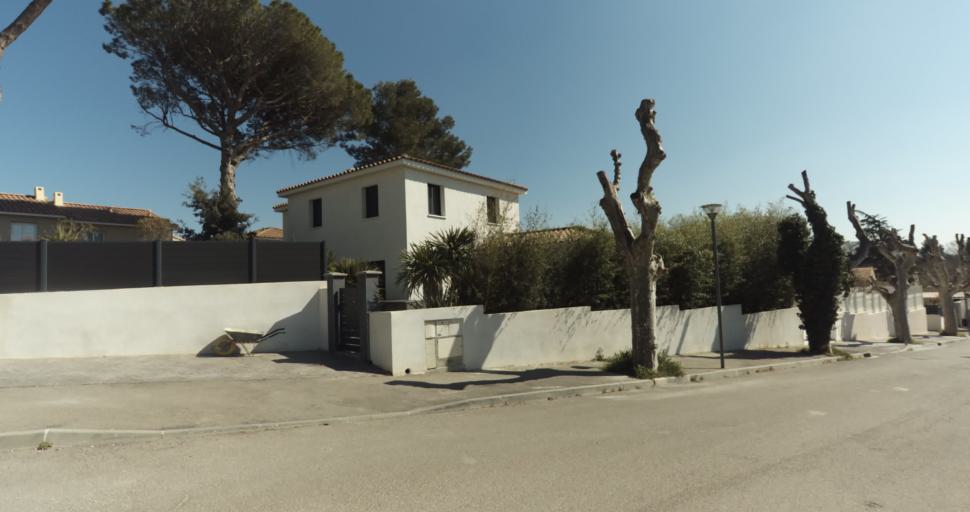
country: FR
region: Provence-Alpes-Cote d'Azur
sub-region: Departement des Bouches-du-Rhone
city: Pelissanne
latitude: 43.6349
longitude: 5.1615
